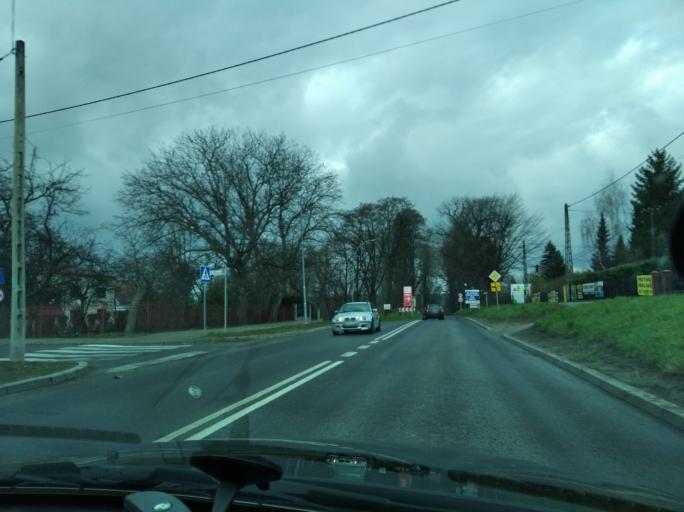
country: PL
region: Subcarpathian Voivodeship
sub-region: Powiat lancucki
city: Lancut
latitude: 50.0760
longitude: 22.2364
